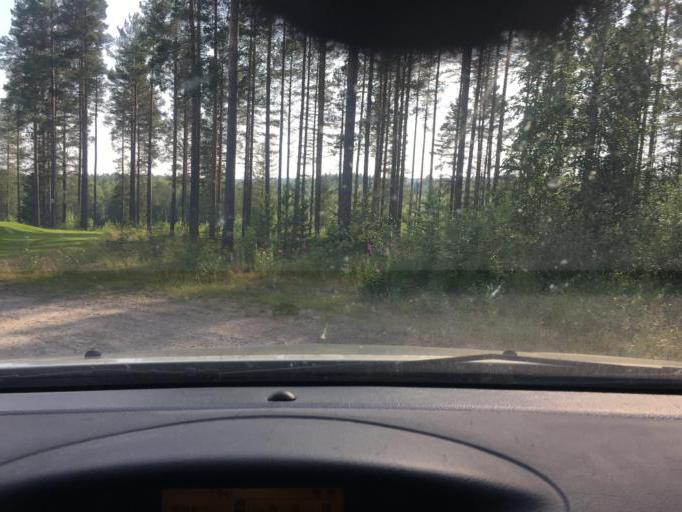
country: SE
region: Norrbotten
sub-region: Kalix Kommun
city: Toere
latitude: 66.0652
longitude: 22.6973
